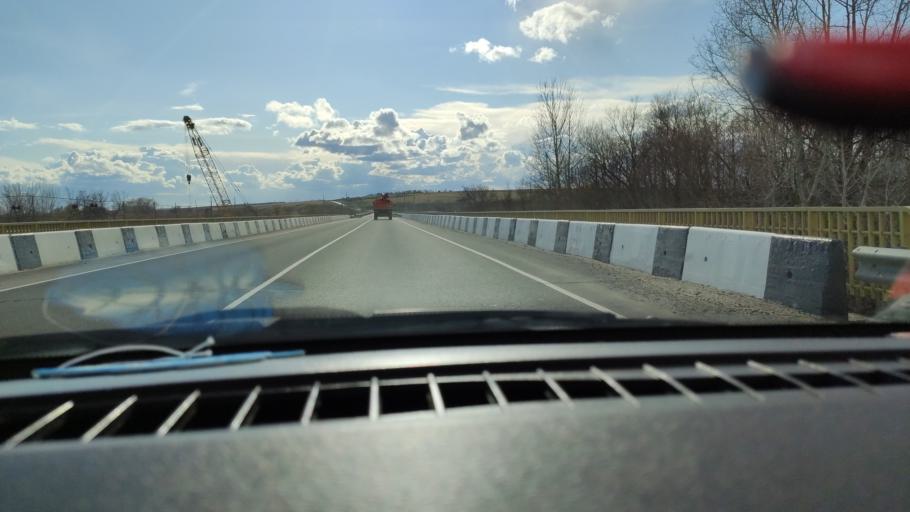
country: RU
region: Saratov
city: Sennoy
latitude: 52.1428
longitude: 46.8975
